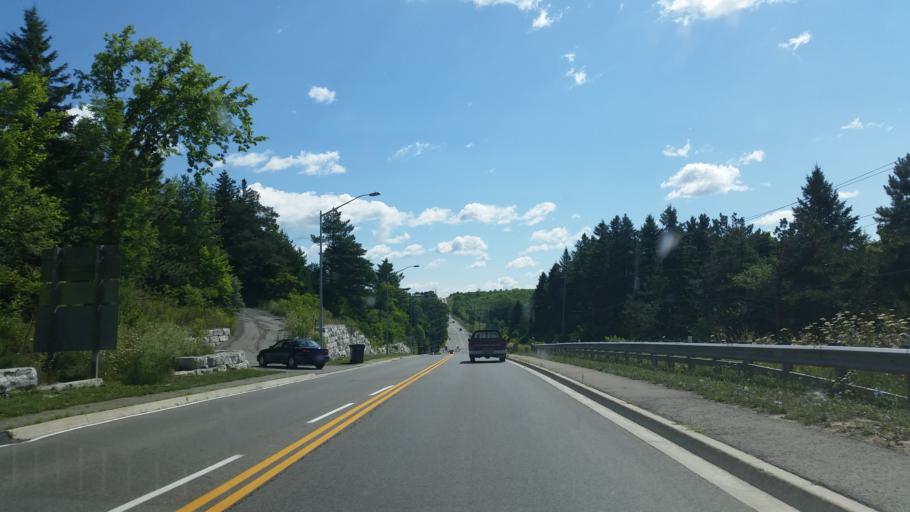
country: CA
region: Ontario
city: Brampton
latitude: 43.8872
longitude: -79.7229
